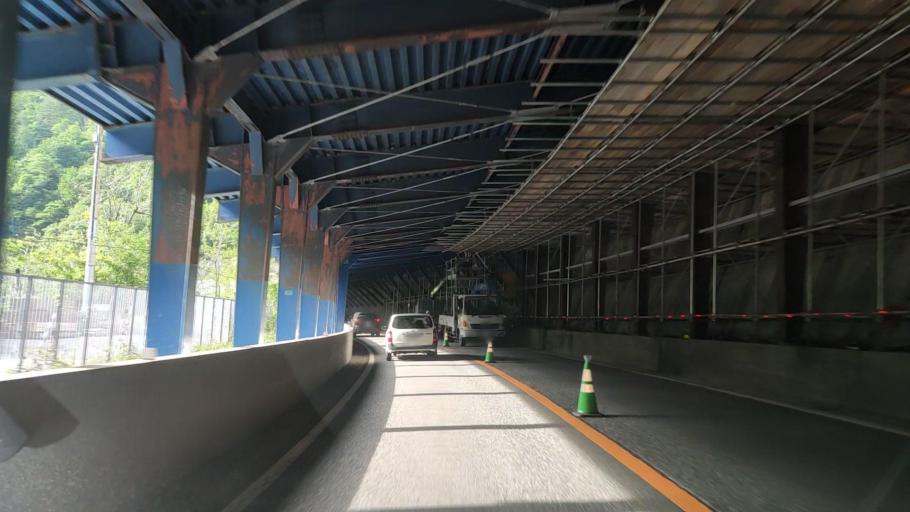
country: JP
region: Gifu
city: Takayama
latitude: 36.3704
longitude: 137.2830
